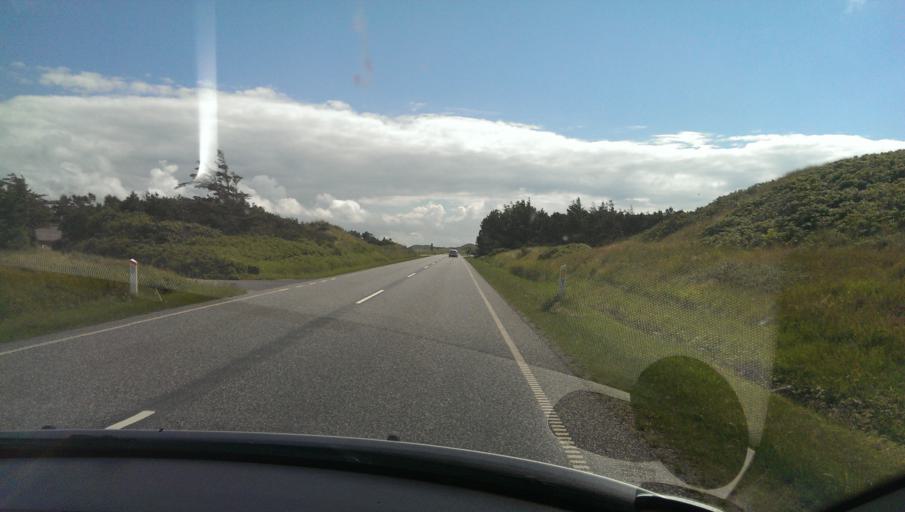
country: DK
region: Central Jutland
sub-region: Holstebro Kommune
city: Ulfborg
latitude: 56.2436
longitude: 8.1394
